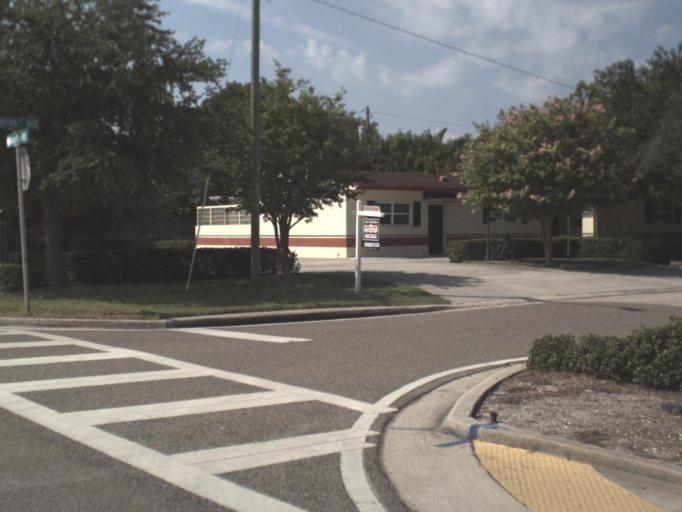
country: US
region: Florida
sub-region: Pinellas County
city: South Pasadena
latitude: 27.7504
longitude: -82.7556
